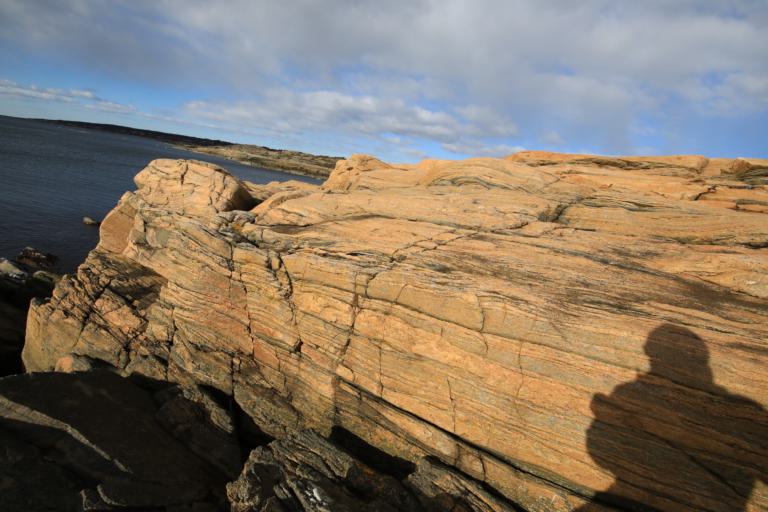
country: SE
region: Halland
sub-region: Kungsbacka Kommun
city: Frillesas
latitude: 57.2174
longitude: 12.1326
